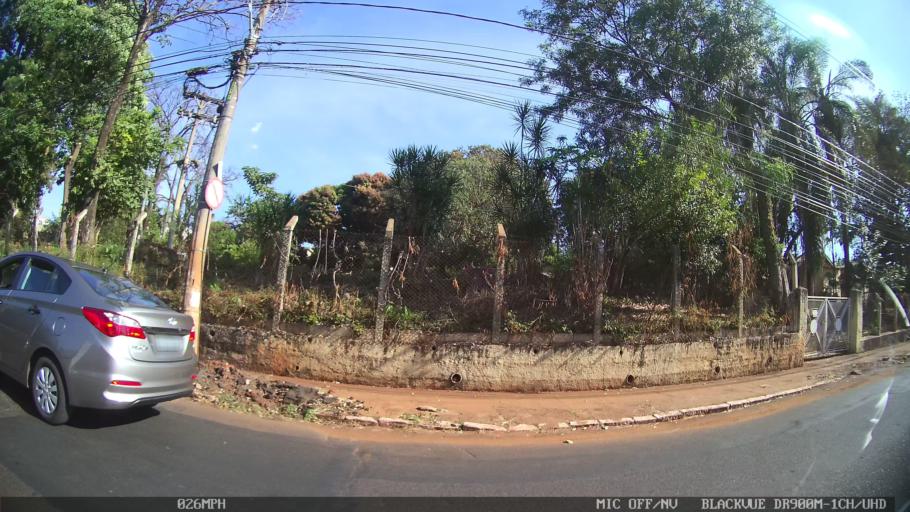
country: BR
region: Sao Paulo
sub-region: Ribeirao Preto
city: Ribeirao Preto
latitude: -21.1718
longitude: -47.7875
